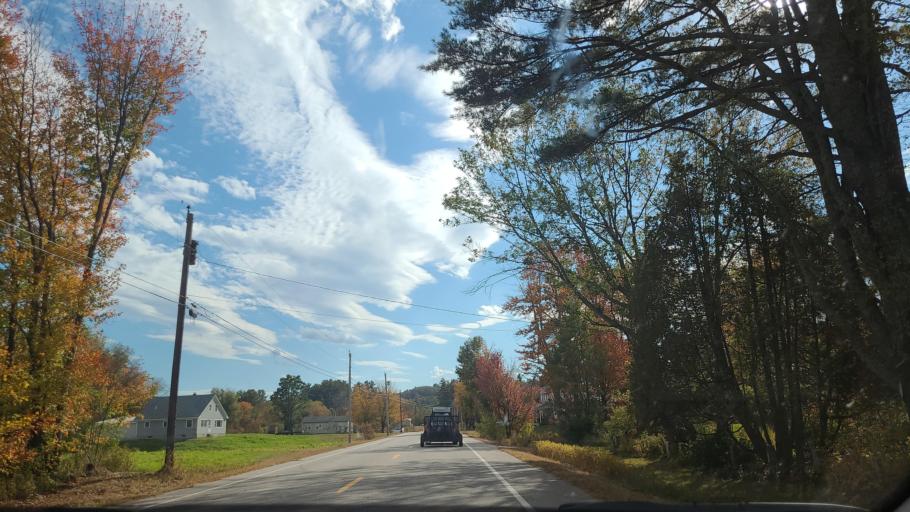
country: US
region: New Hampshire
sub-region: Carroll County
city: Conway
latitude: 44.0152
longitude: -71.1308
